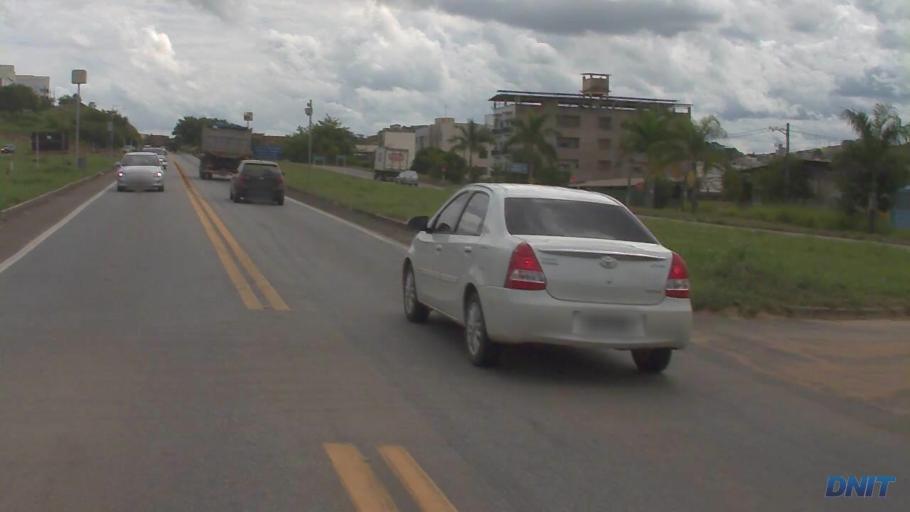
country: BR
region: Minas Gerais
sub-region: Ipatinga
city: Ipatinga
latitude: -19.4544
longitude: -42.5218
